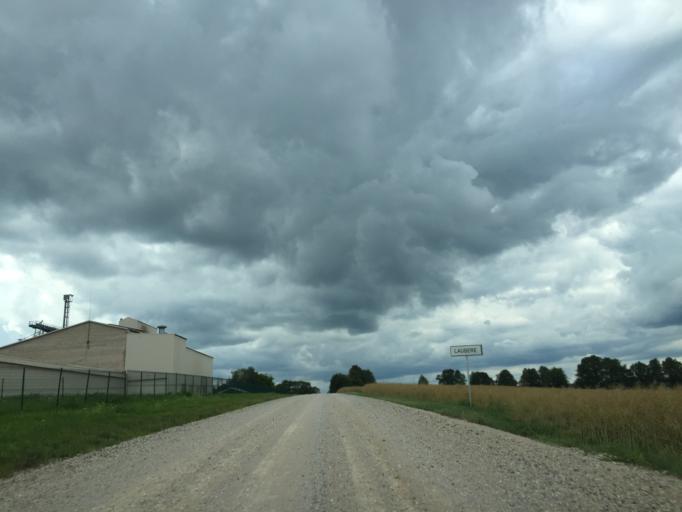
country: LV
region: Malpils
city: Malpils
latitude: 56.8572
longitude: 25.0318
